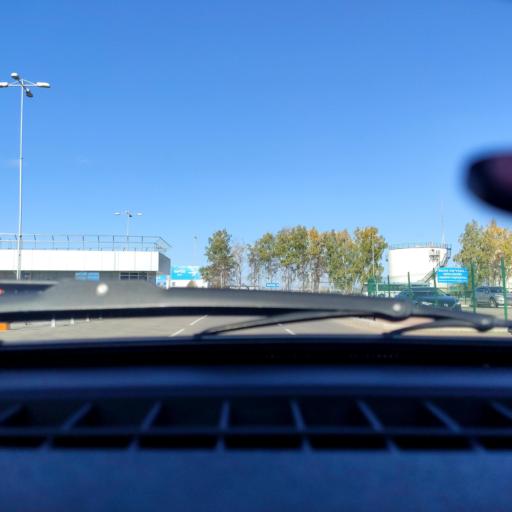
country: RU
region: Bashkortostan
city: Ufa
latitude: 54.5670
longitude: 55.8849
